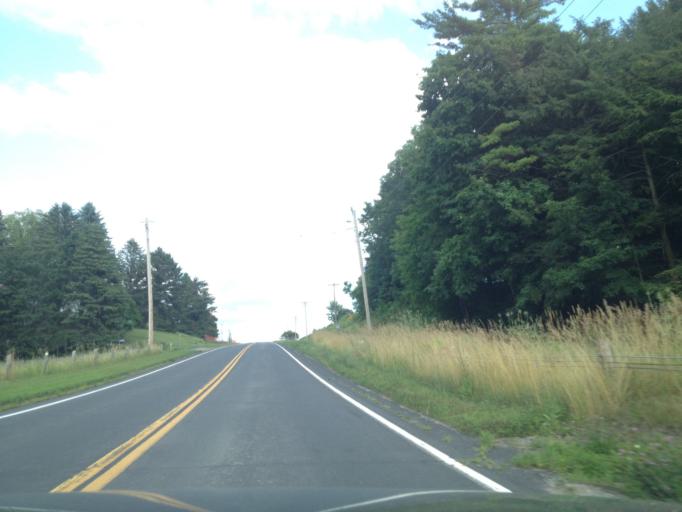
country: CA
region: Ontario
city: Aylmer
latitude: 42.6752
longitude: -80.9527
